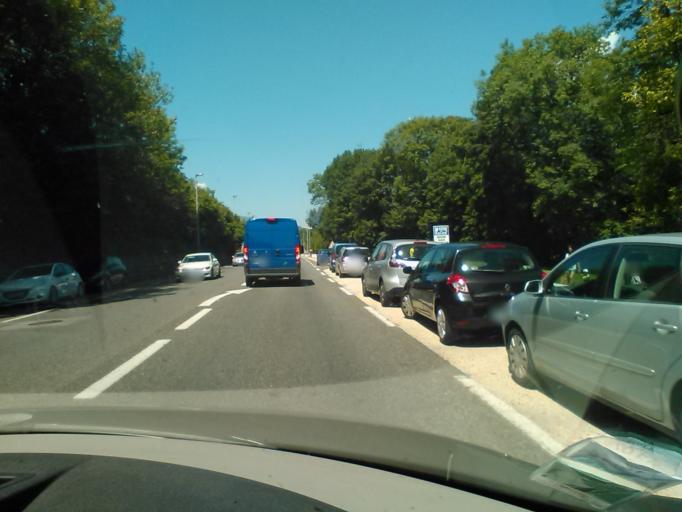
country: FR
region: Rhone-Alpes
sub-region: Departement de la Savoie
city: Challes-les-Eaux
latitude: 45.5533
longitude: 5.9803
